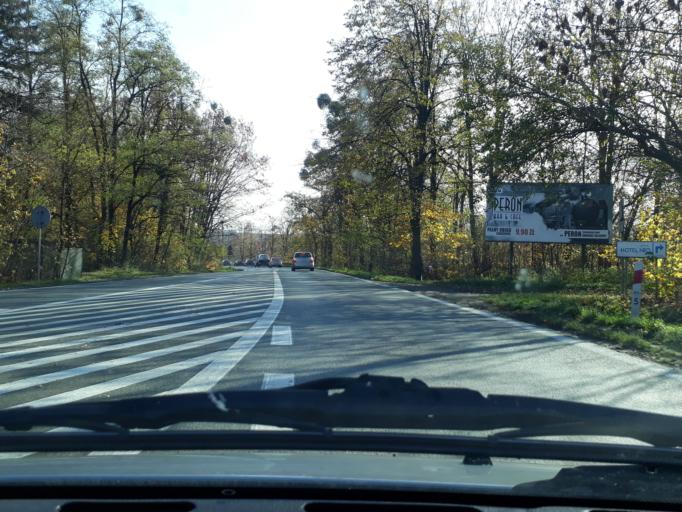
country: PL
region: Silesian Voivodeship
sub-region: Powiat tarnogorski
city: Tarnowskie Gory
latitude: 50.4413
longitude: 18.8359
